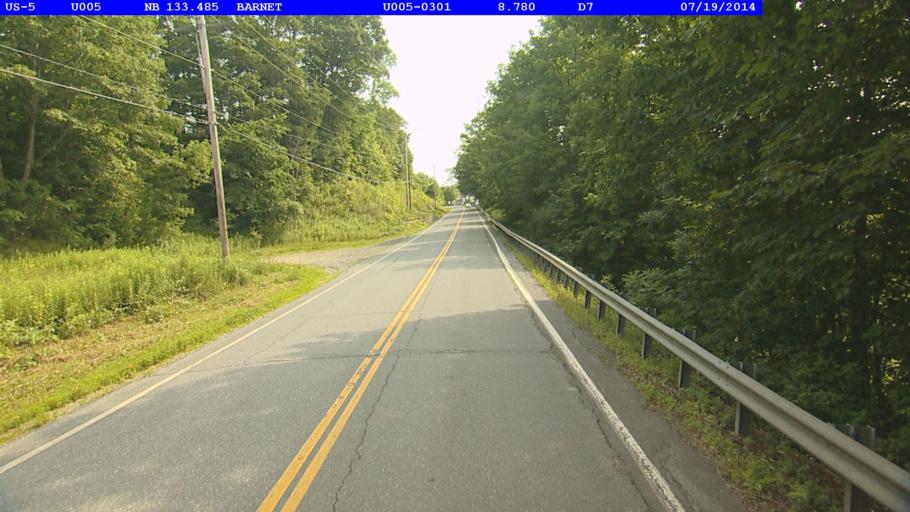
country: US
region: Vermont
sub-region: Caledonia County
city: Saint Johnsbury
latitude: 44.3670
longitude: -72.0383
